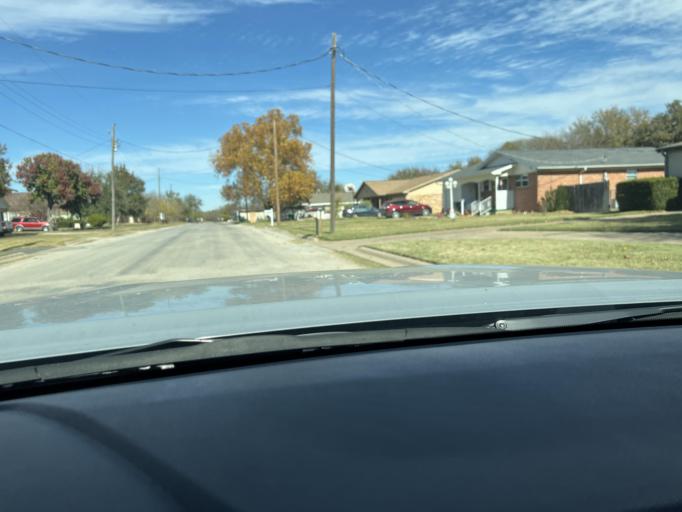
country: US
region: Texas
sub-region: Eastland County
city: Eastland
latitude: 32.3969
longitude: -98.8307
